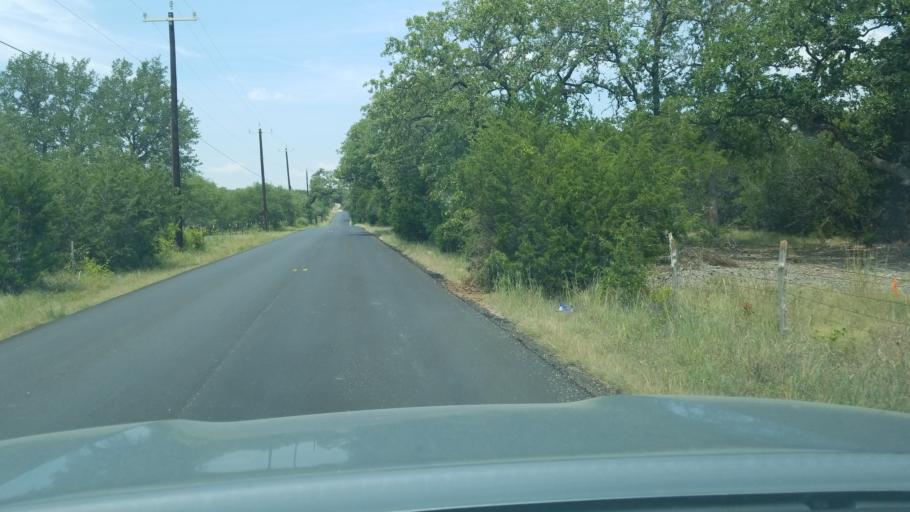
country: US
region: Texas
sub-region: Comal County
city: Bulverde
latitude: 29.7598
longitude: -98.4795
